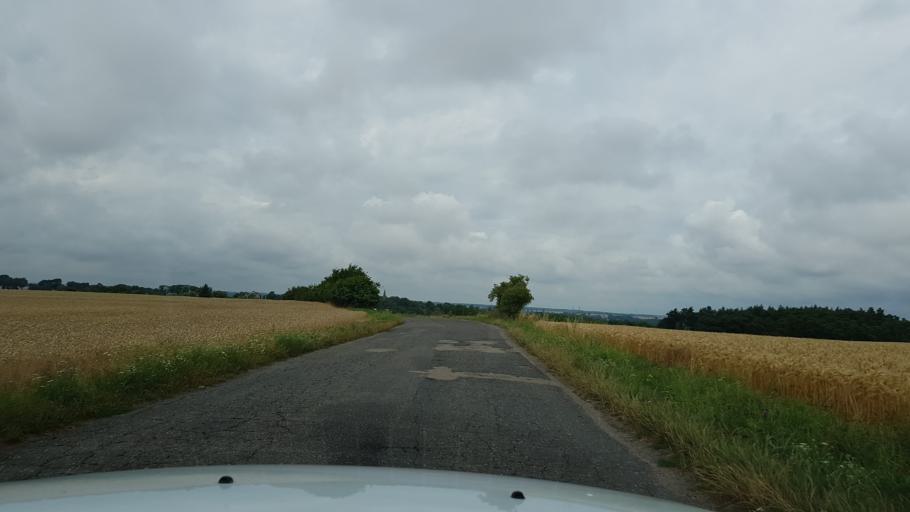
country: PL
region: West Pomeranian Voivodeship
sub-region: Powiat pyrzycki
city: Przelewice
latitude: 53.0973
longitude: 15.1441
